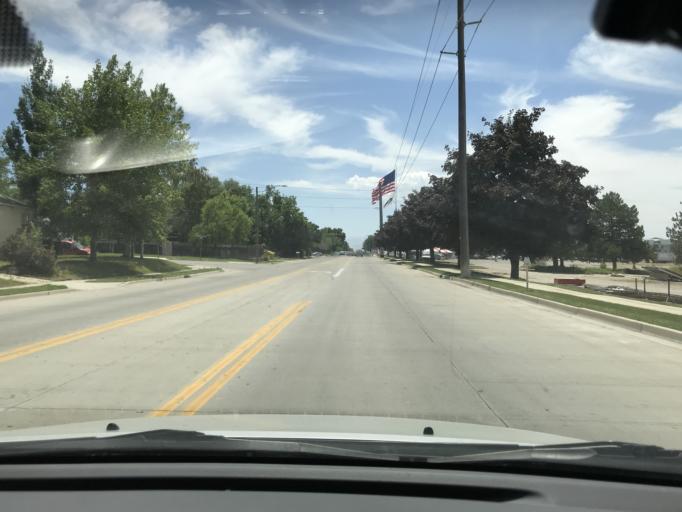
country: US
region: Utah
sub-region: Davis County
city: Woods Cross
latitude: 40.8727
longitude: -111.8874
